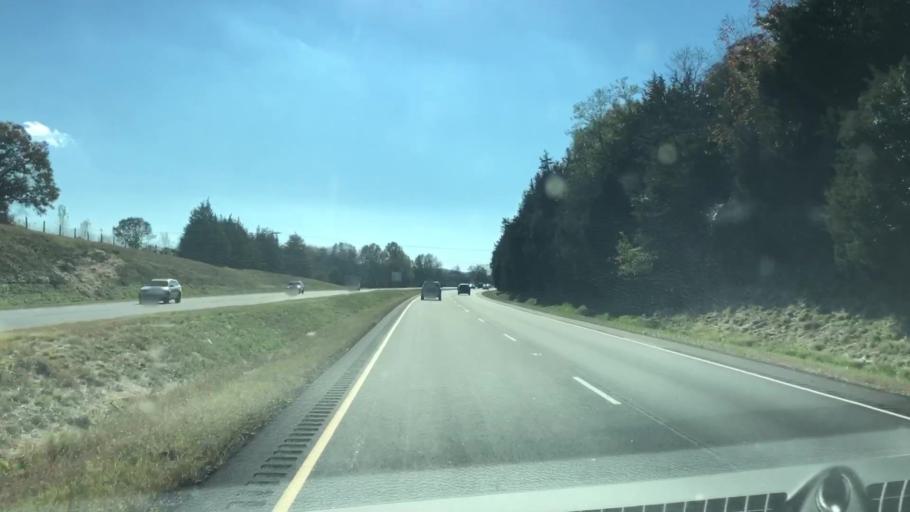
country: US
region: Virginia
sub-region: Culpeper County
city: Culpeper
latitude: 38.4874
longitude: -77.9380
